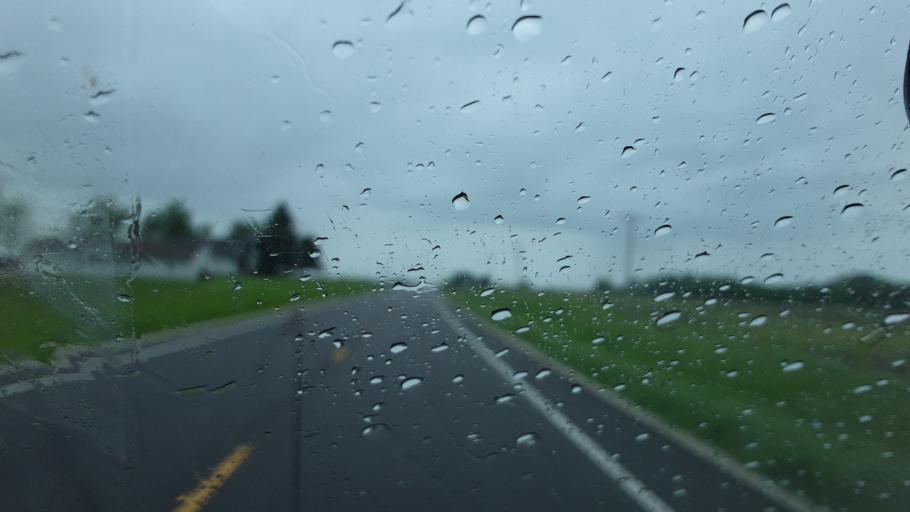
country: US
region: Missouri
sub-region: Monroe County
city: Paris
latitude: 39.4811
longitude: -92.1376
